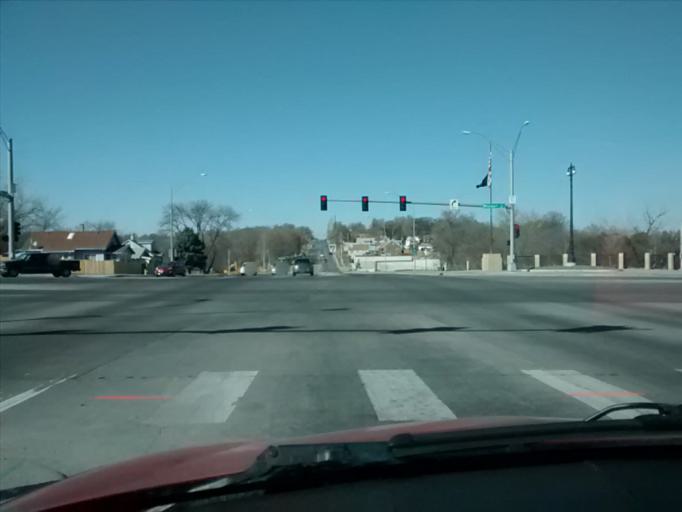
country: US
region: Nebraska
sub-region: Douglas County
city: Omaha
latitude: 41.2127
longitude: -95.9333
